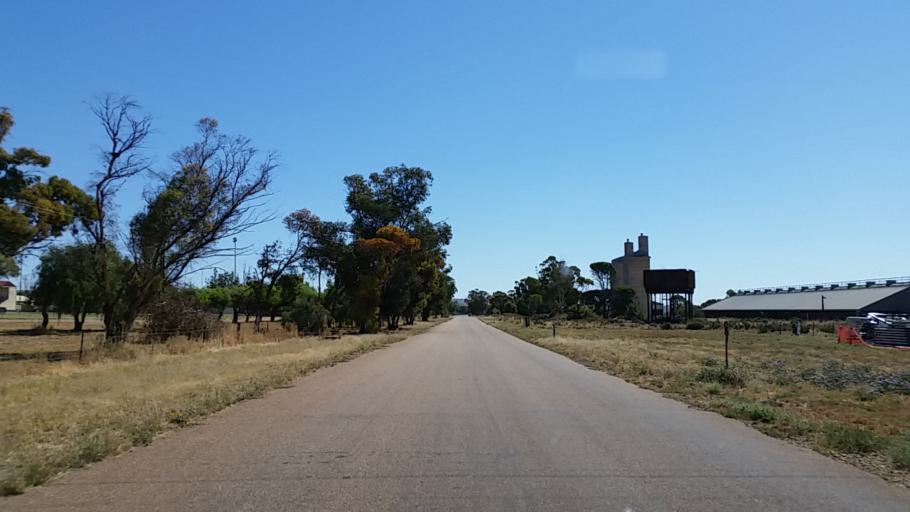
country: AU
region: South Australia
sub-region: Peterborough
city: Peterborough
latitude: -32.7331
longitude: 138.6212
